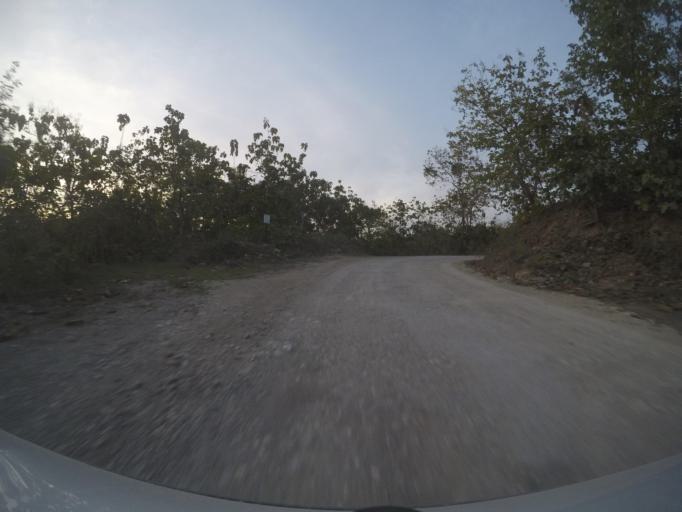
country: TL
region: Viqueque
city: Viqueque
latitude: -8.8926
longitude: 126.3861
